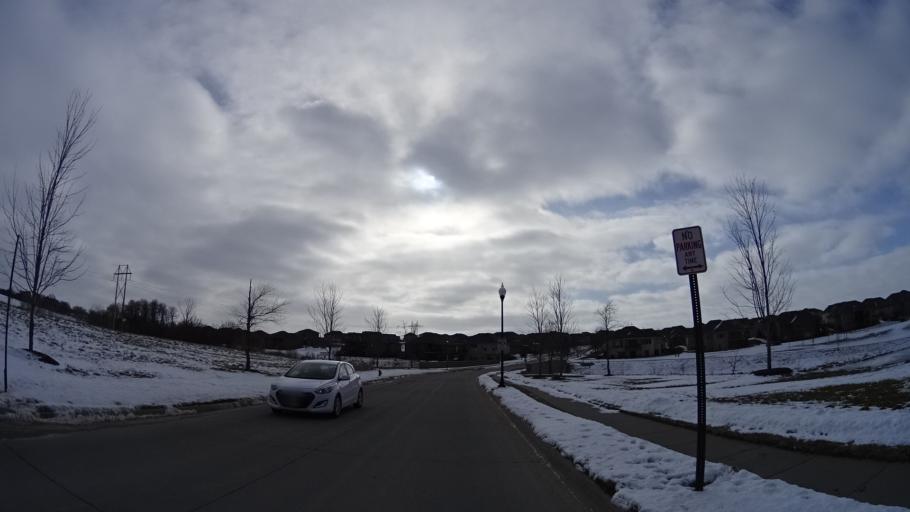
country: US
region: Nebraska
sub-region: Sarpy County
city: Papillion
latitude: 41.1281
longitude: -96.0253
